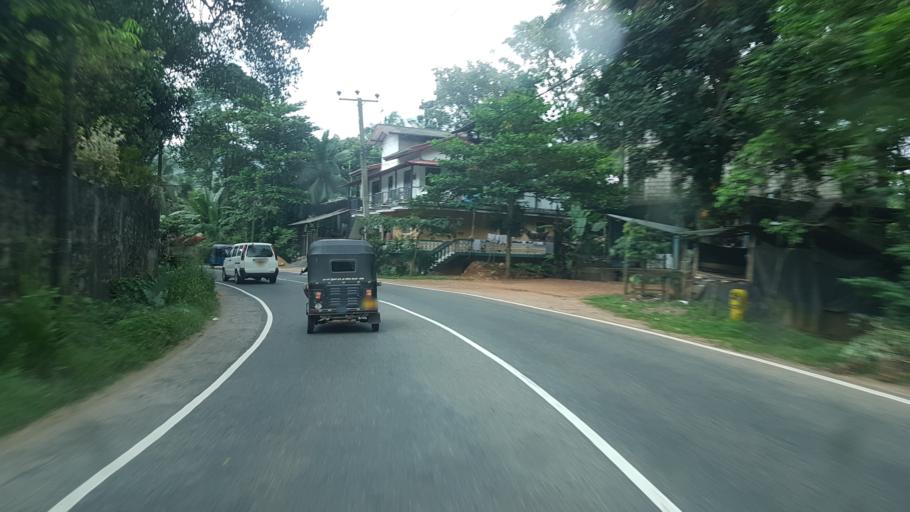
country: LK
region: Western
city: Hanwella Ihala
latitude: 6.9647
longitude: 80.2299
